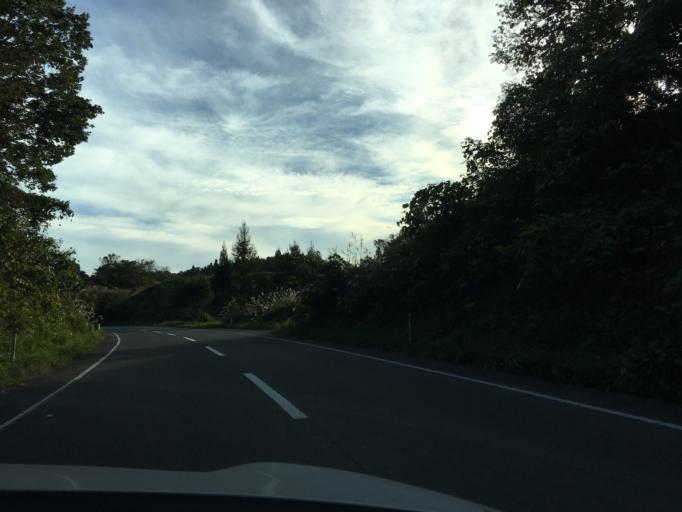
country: JP
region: Fukushima
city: Ishikawa
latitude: 37.2075
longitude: 140.5481
